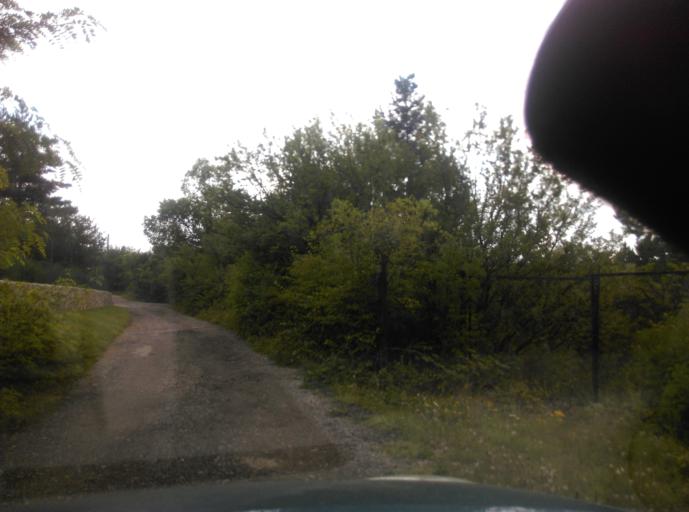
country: BG
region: Sofia-Capital
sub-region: Stolichna Obshtina
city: Sofia
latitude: 42.5881
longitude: 23.3941
